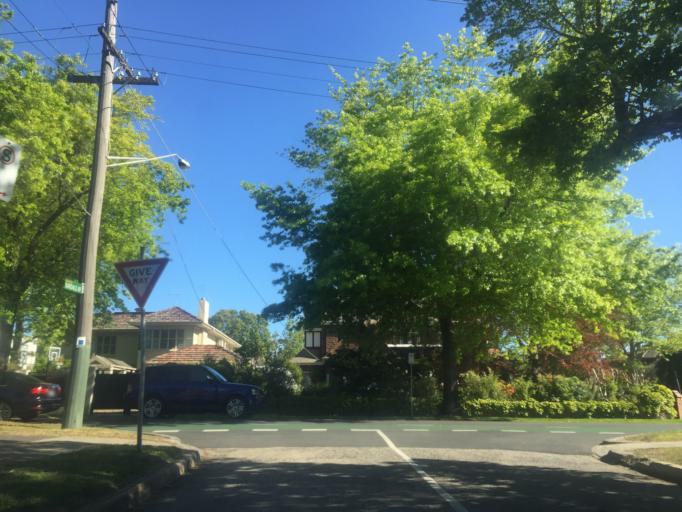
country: AU
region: Victoria
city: Balwyn
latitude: -37.8169
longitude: 145.0701
